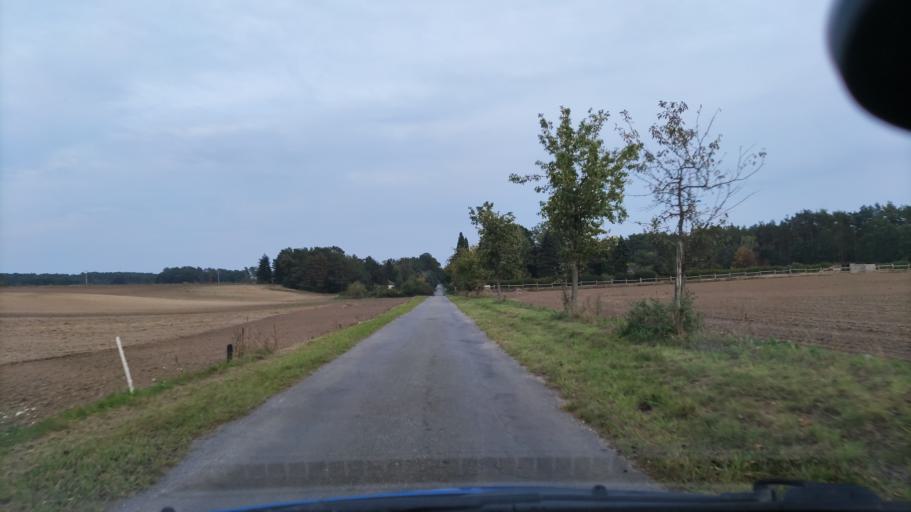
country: DE
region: Lower Saxony
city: Karwitz
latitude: 53.0909
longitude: 10.9902
